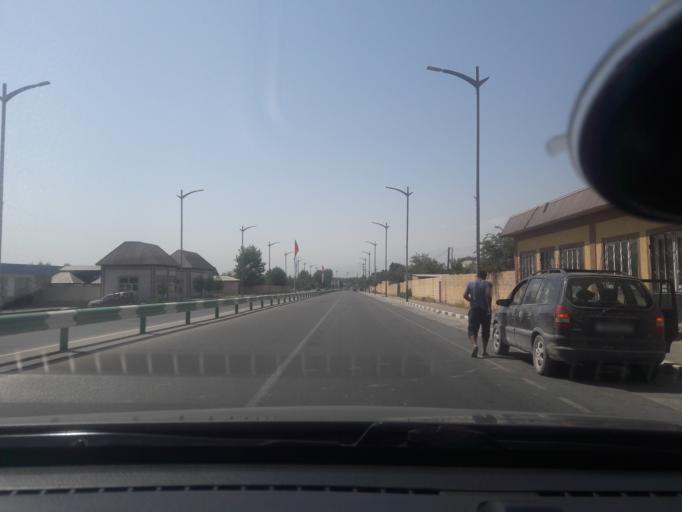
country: TJ
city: Shahrinav
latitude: 38.5624
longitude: 68.4195
